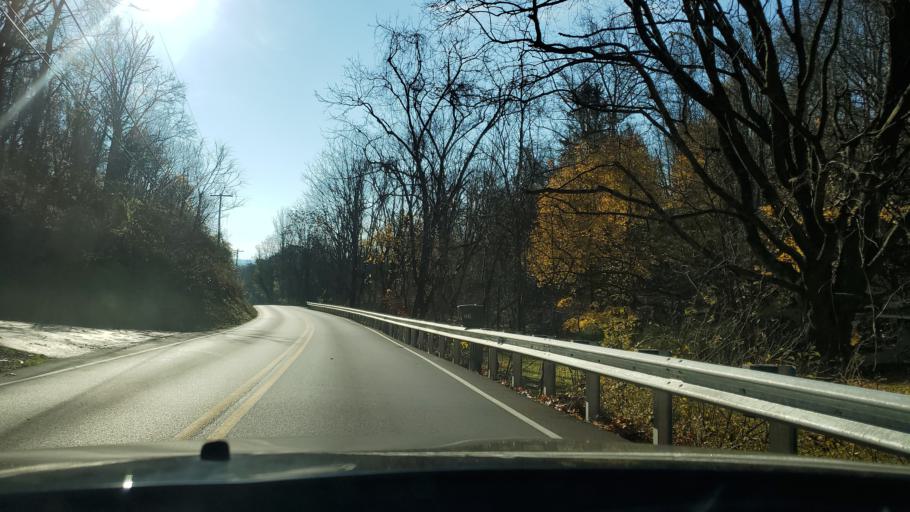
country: US
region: Pennsylvania
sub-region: Cumberland County
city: Mechanicsburg
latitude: 40.1684
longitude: -76.9859
